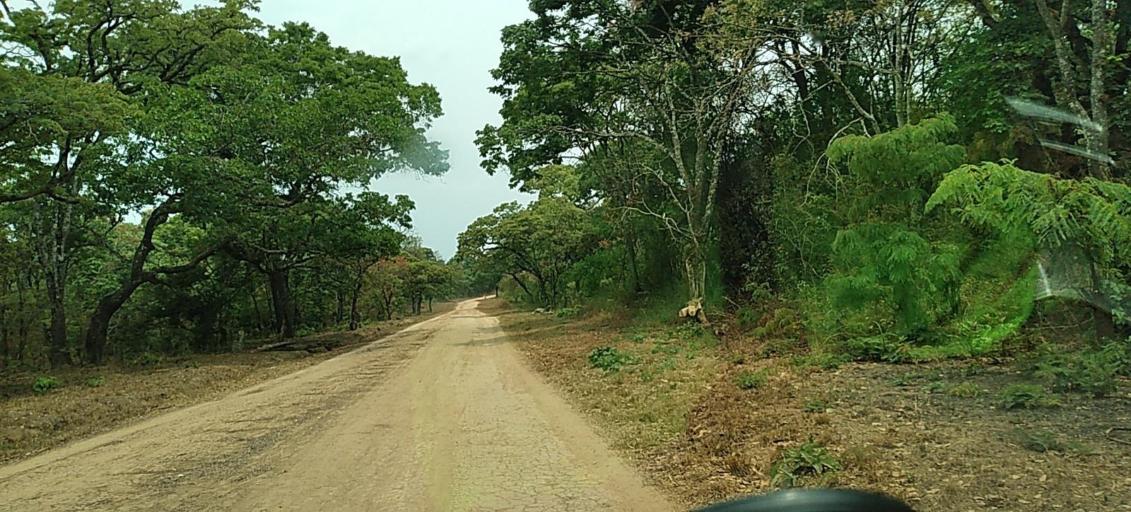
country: ZM
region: North-Western
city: Solwezi
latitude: -12.8231
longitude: 26.5372
